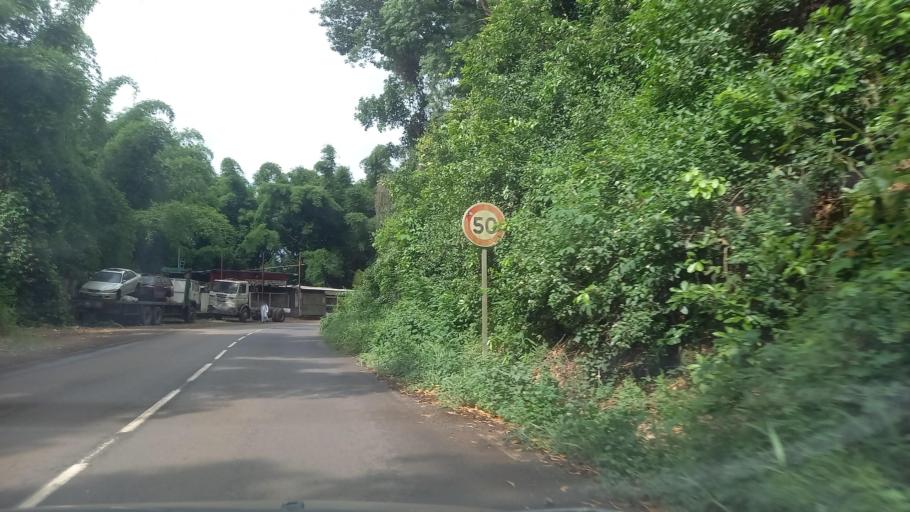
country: YT
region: Ouangani
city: Ouangani
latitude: -12.8394
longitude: 45.1275
